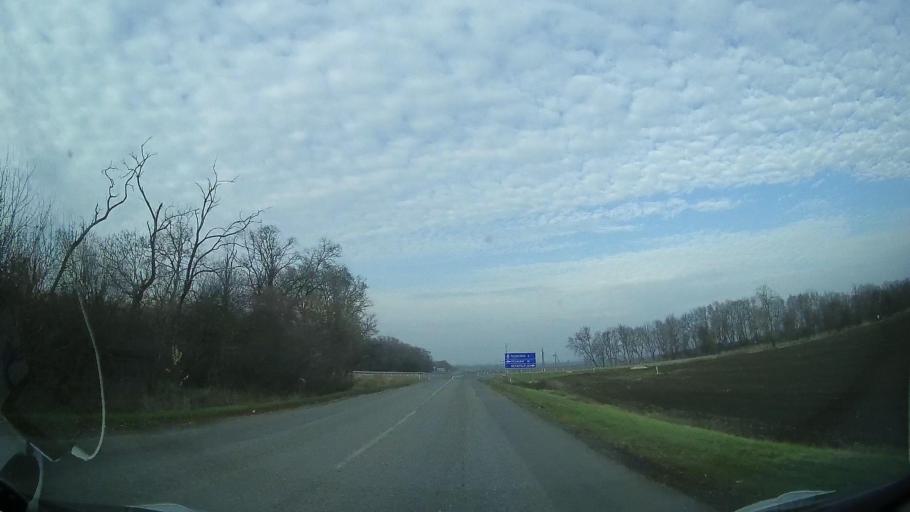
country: RU
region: Rostov
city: Bagayevskaya
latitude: 47.0913
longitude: 40.3915
